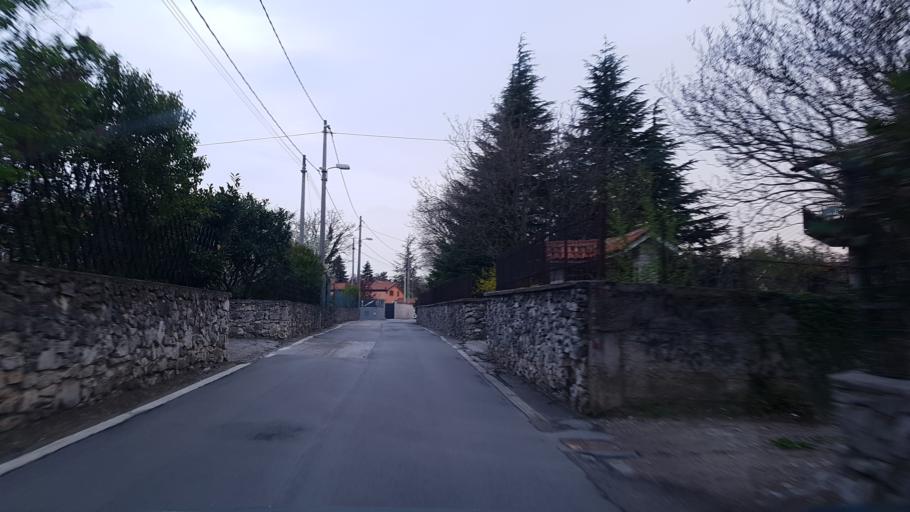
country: IT
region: Friuli Venezia Giulia
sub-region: Provincia di Trieste
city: Domio
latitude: 45.6551
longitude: 13.8399
